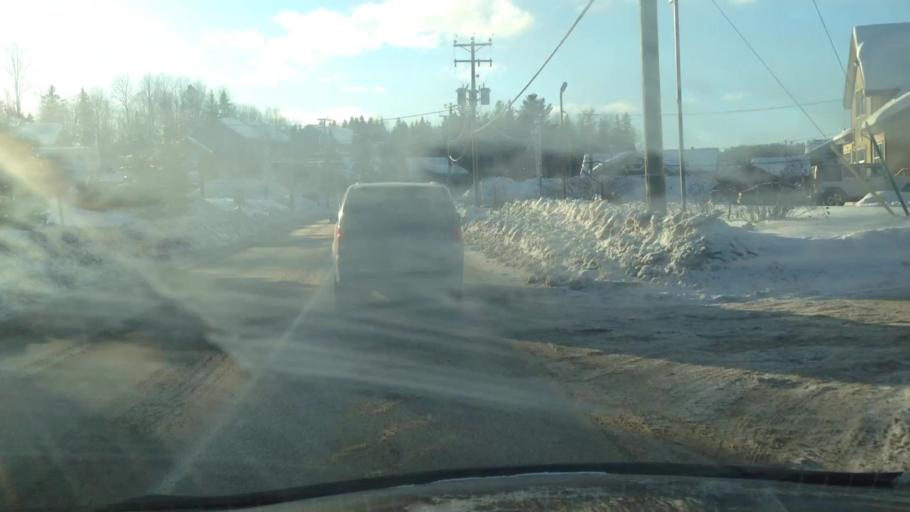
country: CA
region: Quebec
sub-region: Laurentides
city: Saint-Sauveur
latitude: 45.8889
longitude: -74.1439
